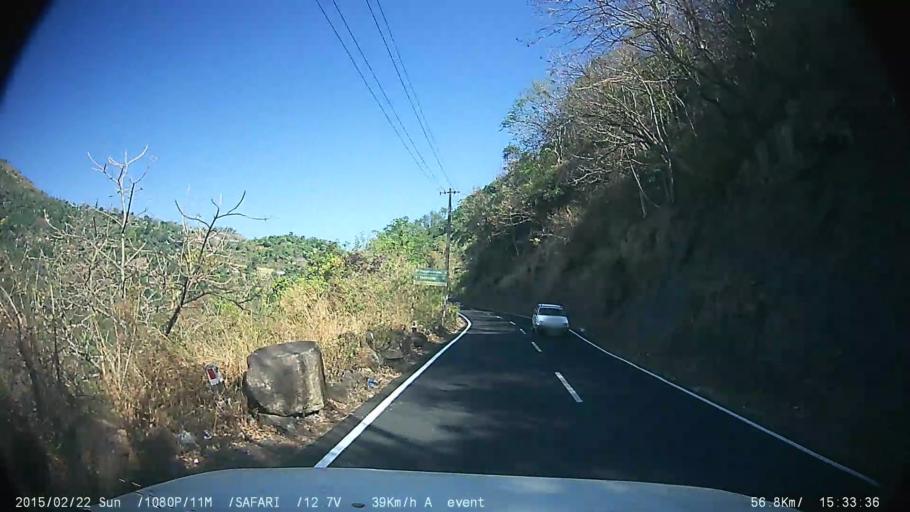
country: IN
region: Kerala
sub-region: Kottayam
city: Erattupetta
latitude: 9.5553
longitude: 76.9665
